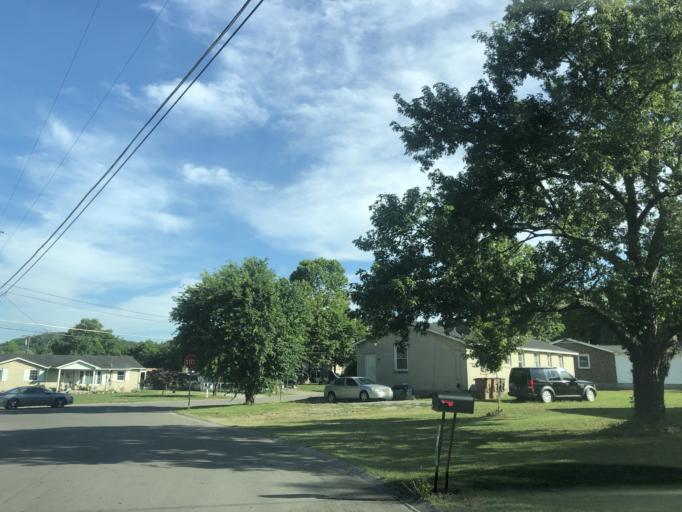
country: US
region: Tennessee
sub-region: Davidson County
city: Nashville
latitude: 36.2169
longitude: -86.8355
